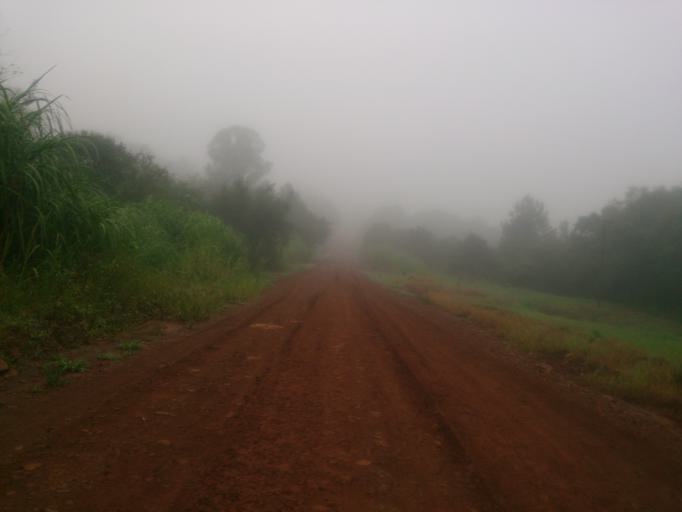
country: AR
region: Misiones
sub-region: Departamento de Obera
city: Obera
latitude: -27.4635
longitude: -55.1062
